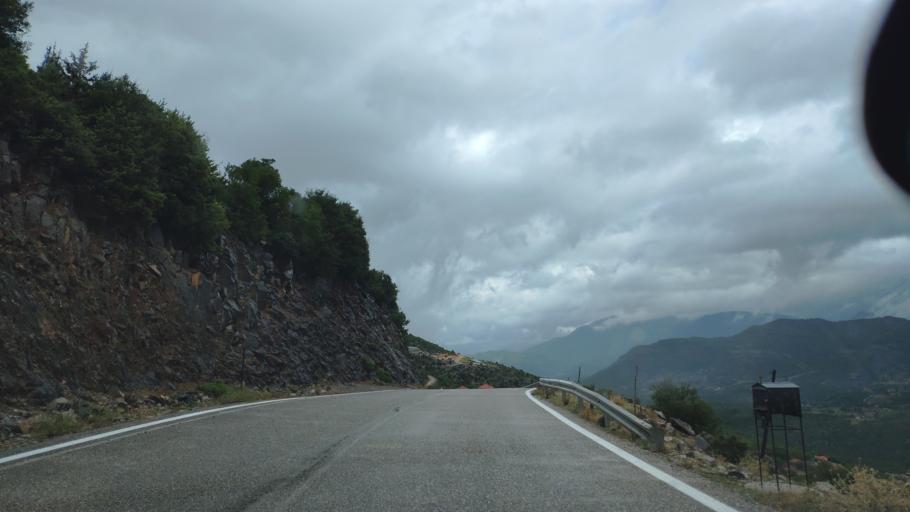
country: GR
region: Thessaly
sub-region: Nomos Kardhitsas
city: Anthiro
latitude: 39.1050
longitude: 21.4089
